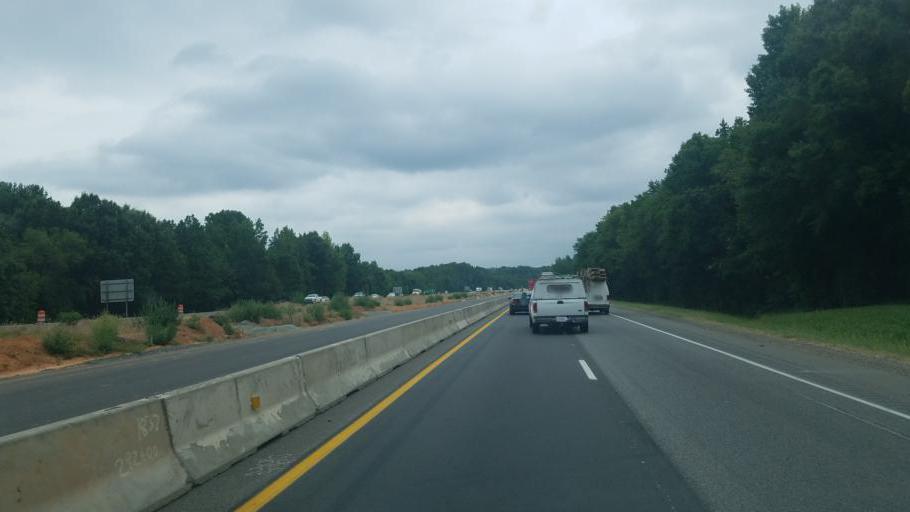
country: US
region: North Carolina
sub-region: Mecklenburg County
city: Cornelius
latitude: 35.4546
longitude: -80.8717
